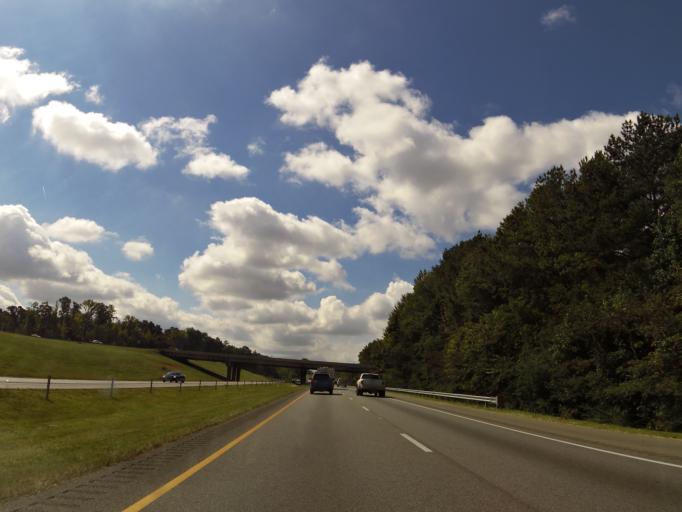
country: US
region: Alabama
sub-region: Jefferson County
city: Bessemer
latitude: 33.3880
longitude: -86.9872
